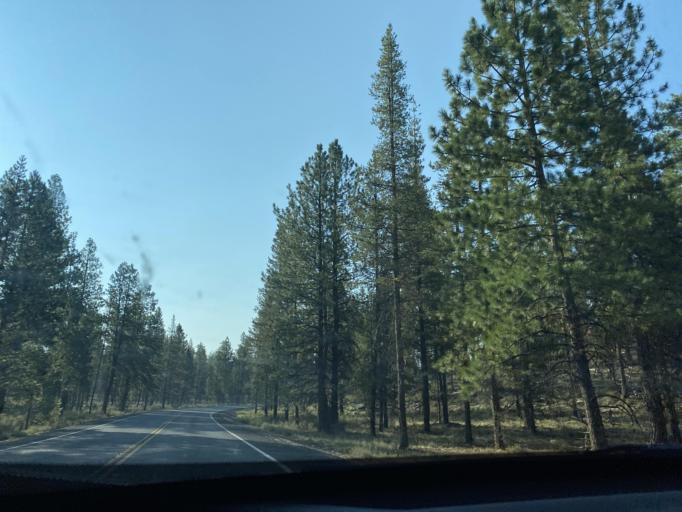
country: US
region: Oregon
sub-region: Deschutes County
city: La Pine
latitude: 43.7106
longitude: -121.4090
